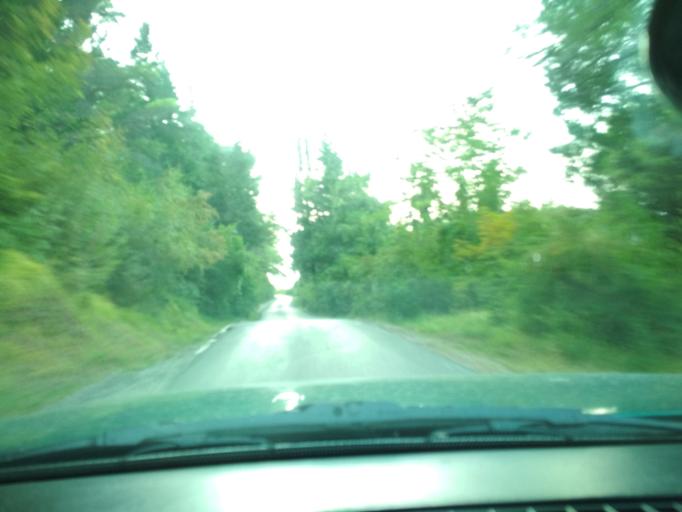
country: ME
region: Kotor
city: Kotor
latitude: 42.3979
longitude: 18.7661
